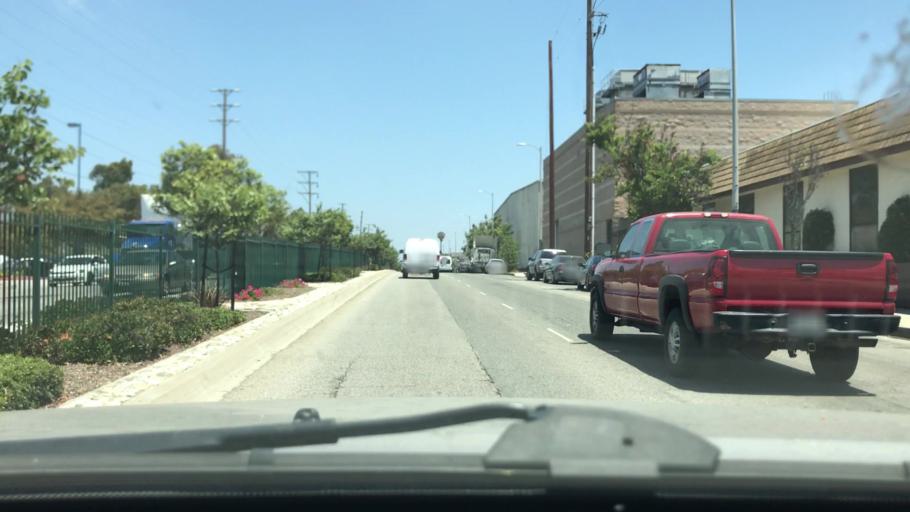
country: US
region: California
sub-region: Los Angeles County
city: West Carson
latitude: 33.8391
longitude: -118.3092
